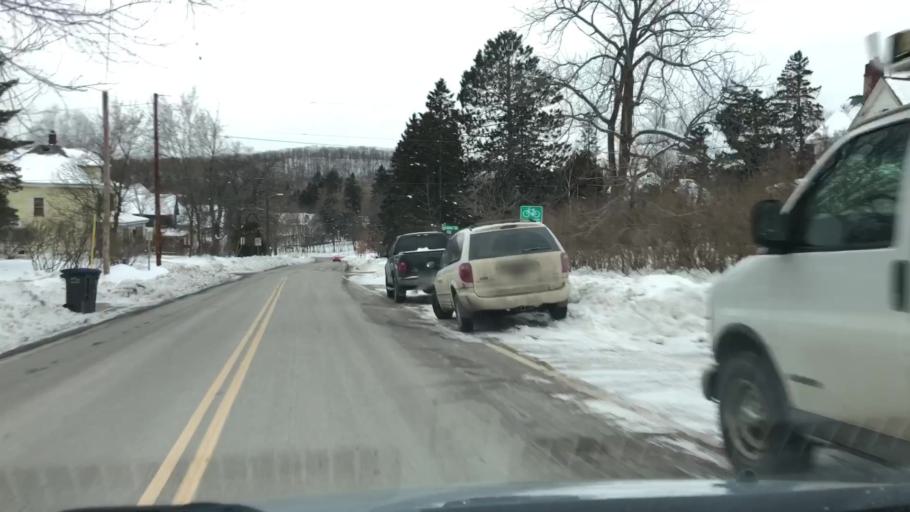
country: US
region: Minnesota
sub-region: Saint Louis County
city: Arnold
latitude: 46.8339
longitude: -92.0682
